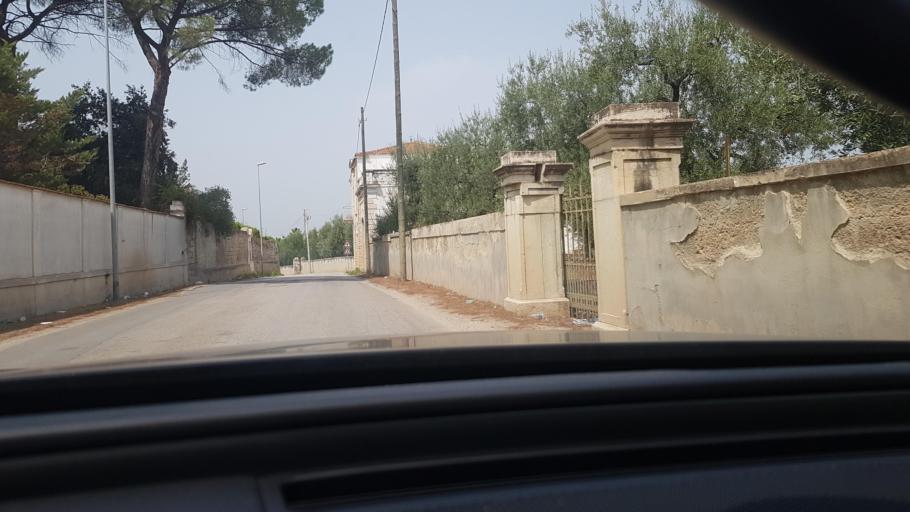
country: IT
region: Apulia
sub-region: Provincia di Barletta - Andria - Trani
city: Andria
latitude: 41.2324
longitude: 16.2712
